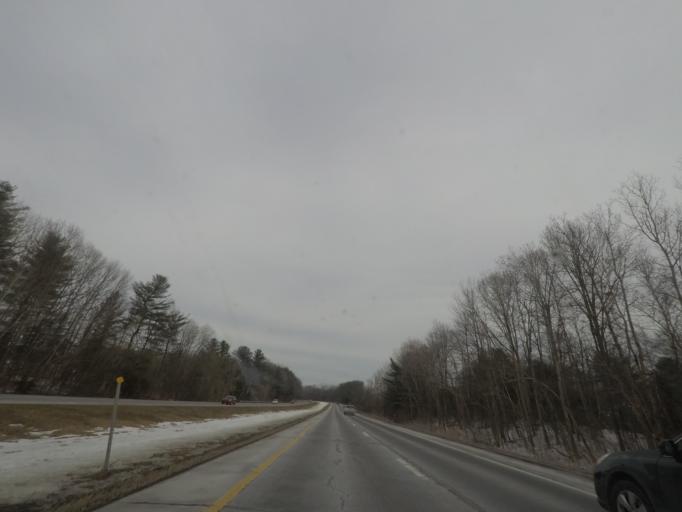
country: US
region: New York
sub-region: Albany County
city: Delmar
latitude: 42.6053
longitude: -73.8307
